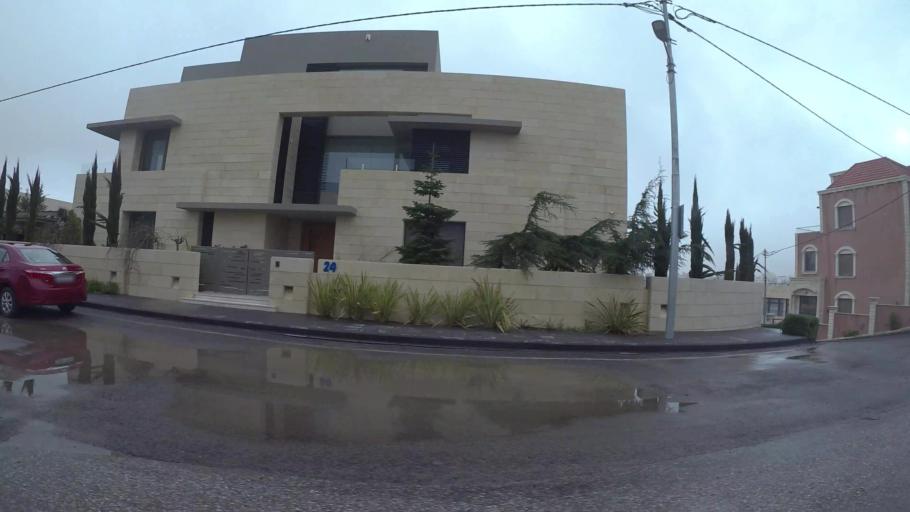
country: JO
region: Amman
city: Al Jubayhah
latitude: 32.0075
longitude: 35.8217
